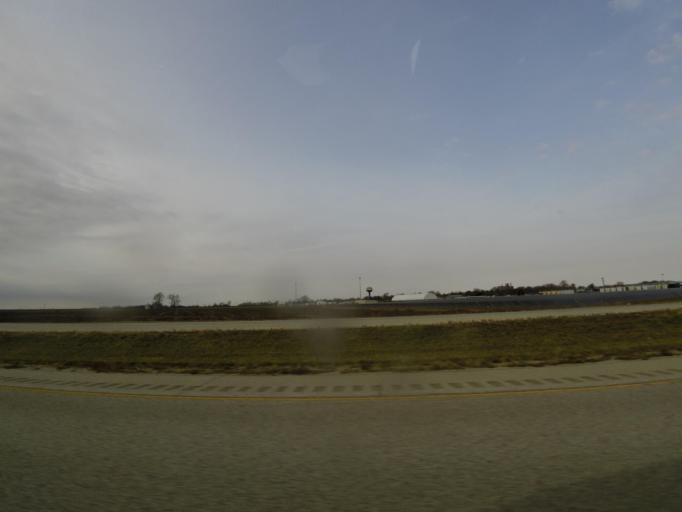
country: US
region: Illinois
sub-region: Christian County
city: Assumption
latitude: 39.5115
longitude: -89.0364
